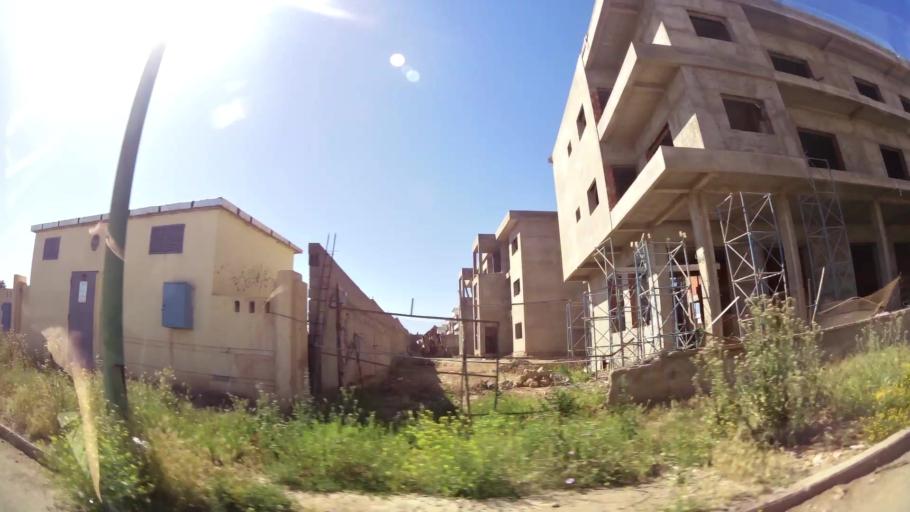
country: MA
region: Oriental
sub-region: Oujda-Angad
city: Oujda
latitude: 34.7184
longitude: -1.9168
